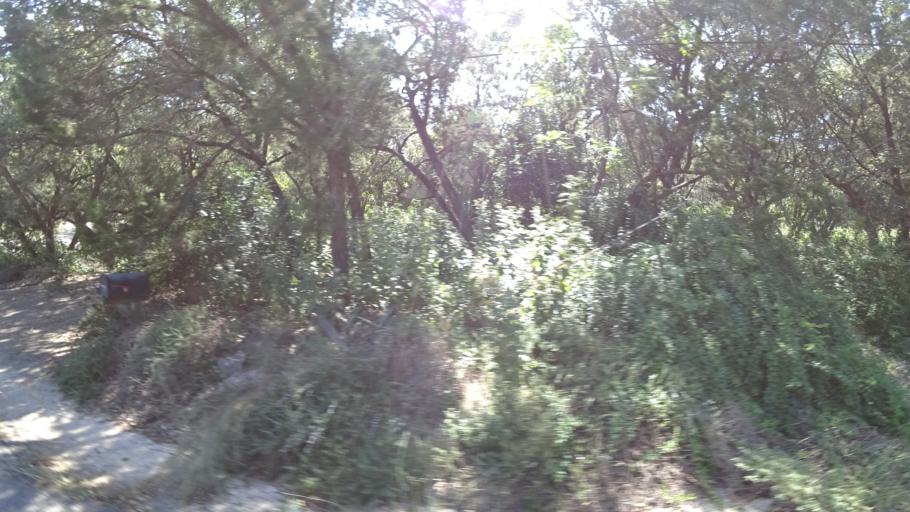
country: US
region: Texas
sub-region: Travis County
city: West Lake Hills
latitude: 30.3058
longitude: -97.8000
